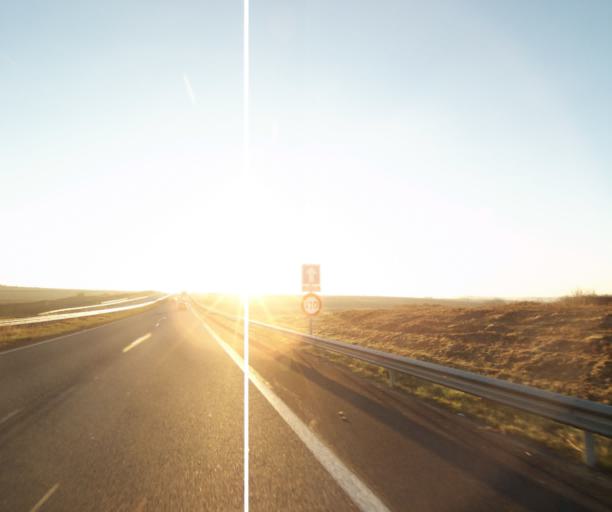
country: FR
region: Poitou-Charentes
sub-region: Departement de la Charente-Maritime
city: Cherac
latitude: 45.7069
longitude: -0.4818
